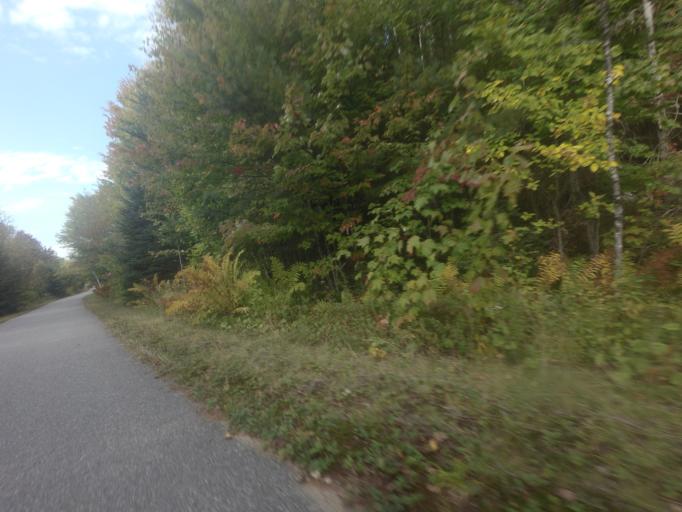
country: CA
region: Quebec
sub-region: Laurentides
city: Labelle
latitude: 46.2834
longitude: -74.7444
